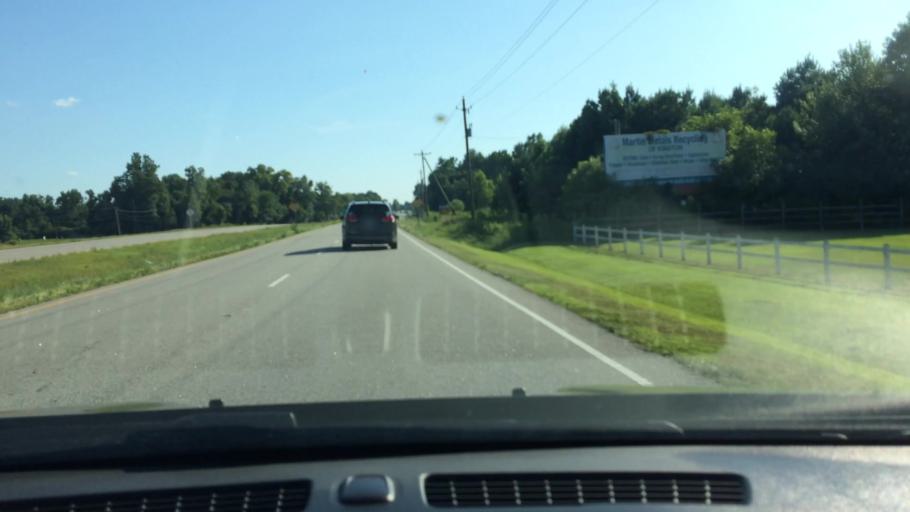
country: US
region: North Carolina
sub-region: Lenoir County
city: Kinston
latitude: 35.2992
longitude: -77.5362
